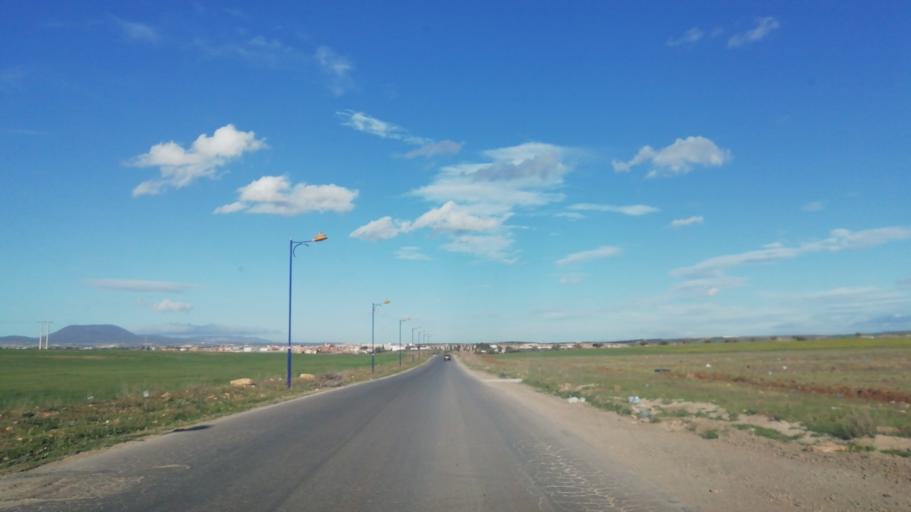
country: DZ
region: Oran
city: Sidi ech Chahmi
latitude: 35.6448
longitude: -0.5351
